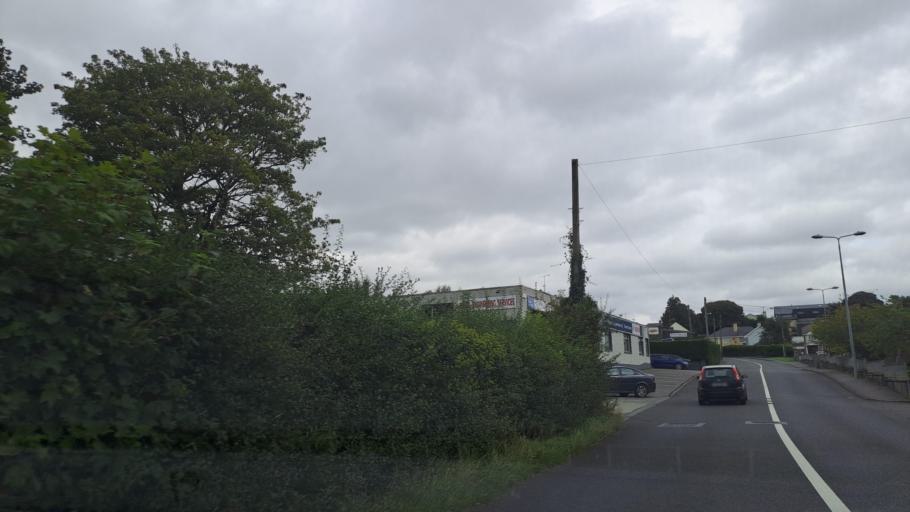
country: IE
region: Ulster
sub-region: An Cabhan
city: Bailieborough
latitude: 53.9927
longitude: -6.9002
